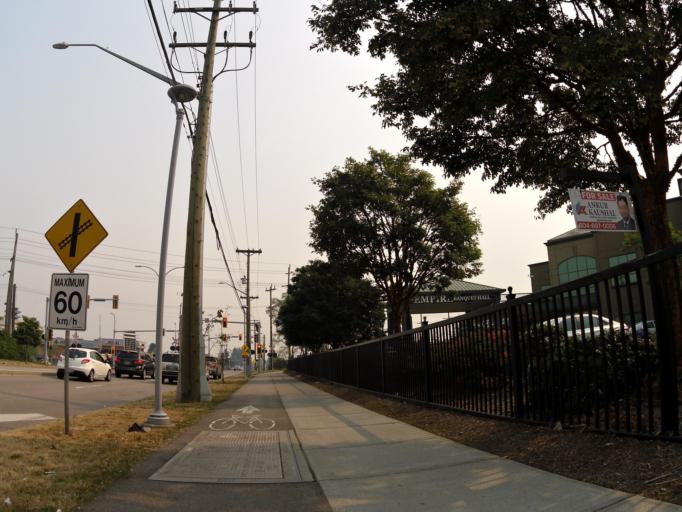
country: CA
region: British Columbia
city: Delta
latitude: 49.1482
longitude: -122.8662
